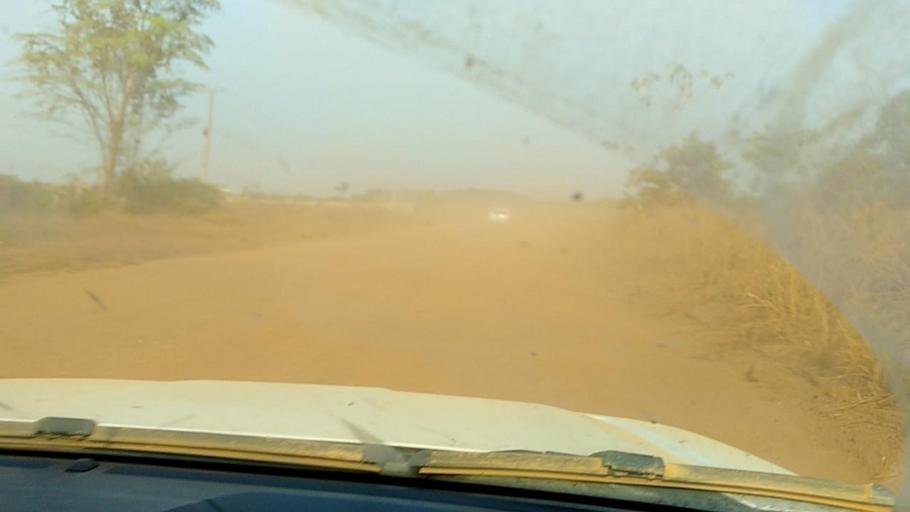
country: BR
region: Rondonia
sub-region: Porto Velho
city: Porto Velho
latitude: -8.7596
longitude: -63.9747
